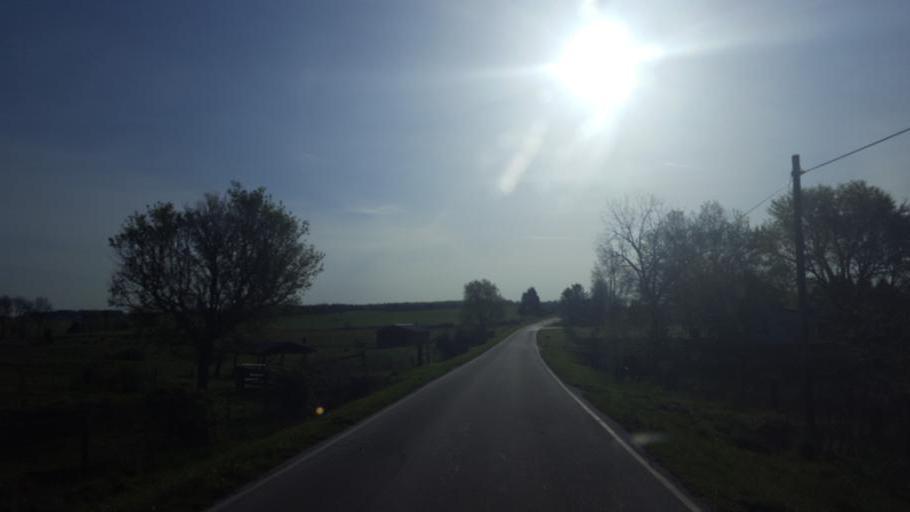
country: US
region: Kentucky
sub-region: Hart County
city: Munfordville
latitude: 37.4857
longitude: -85.9460
